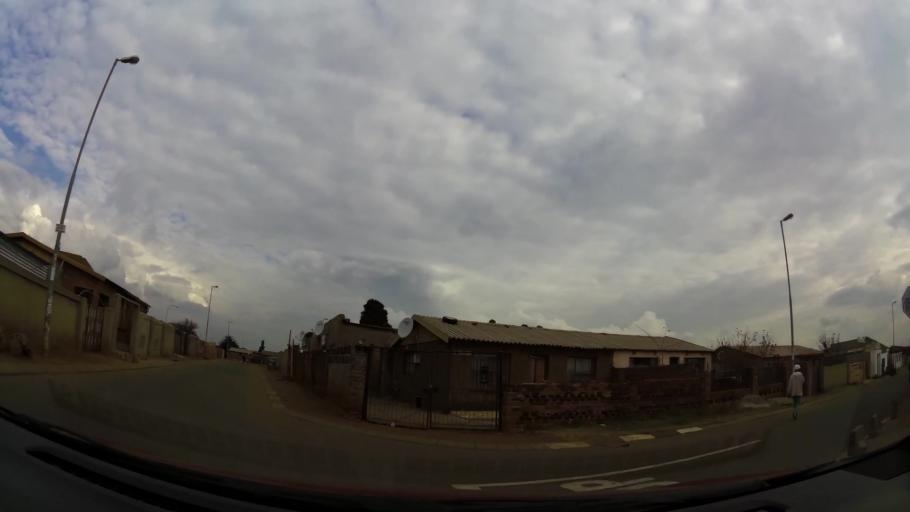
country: ZA
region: Gauteng
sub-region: City of Johannesburg Metropolitan Municipality
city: Soweto
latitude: -26.2476
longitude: 27.8452
